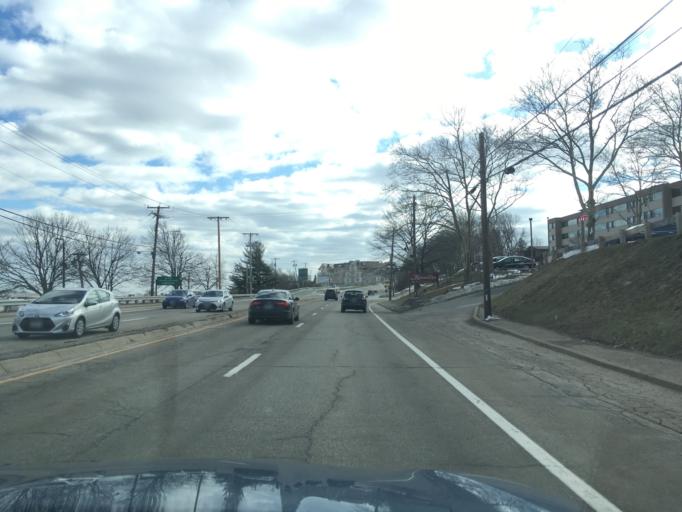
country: US
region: Rhode Island
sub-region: Providence County
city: Cranston
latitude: 41.7619
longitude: -71.4596
